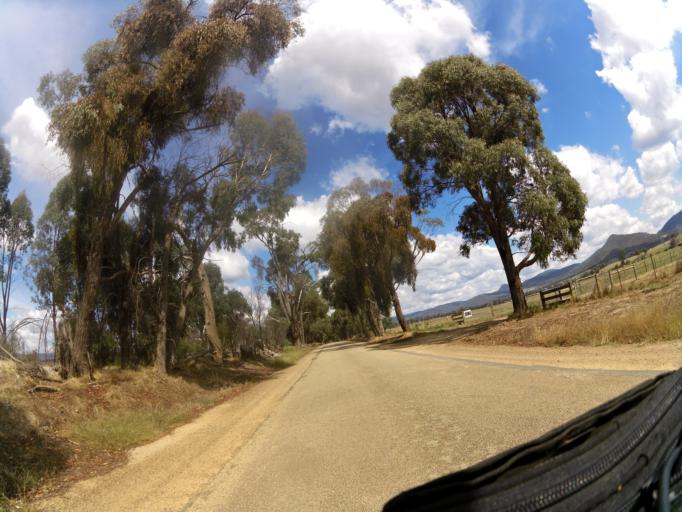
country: AU
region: Victoria
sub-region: Benalla
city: Benalla
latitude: -36.7660
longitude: 145.9761
